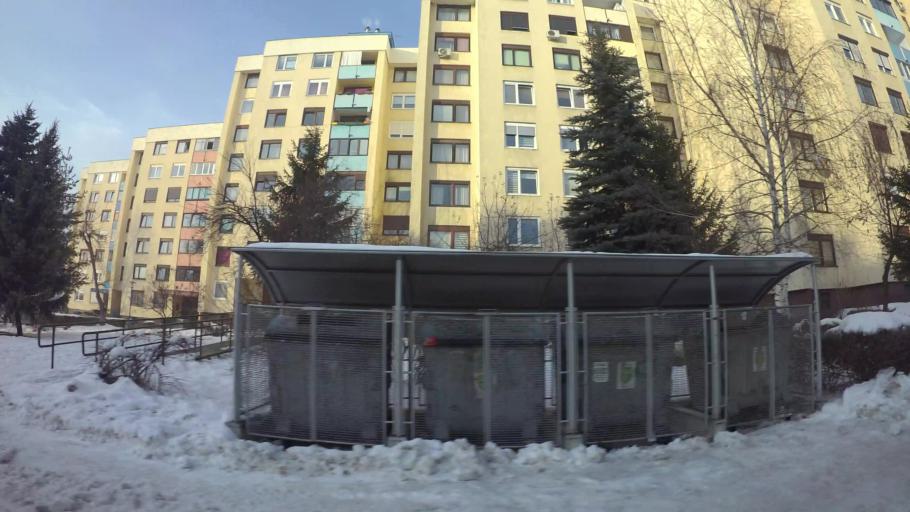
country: BA
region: Federation of Bosnia and Herzegovina
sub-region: Kanton Sarajevo
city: Sarajevo
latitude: 43.8381
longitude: 18.3443
